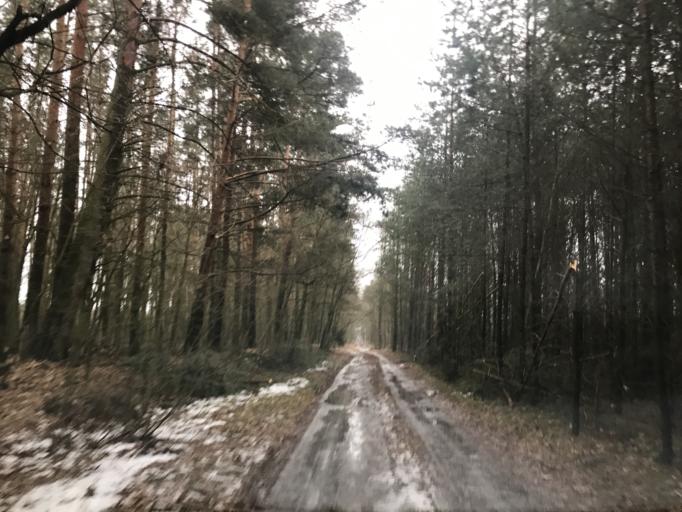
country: PL
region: Kujawsko-Pomorskie
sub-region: Powiat brodnicki
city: Brzozie
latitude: 53.2916
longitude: 19.5646
